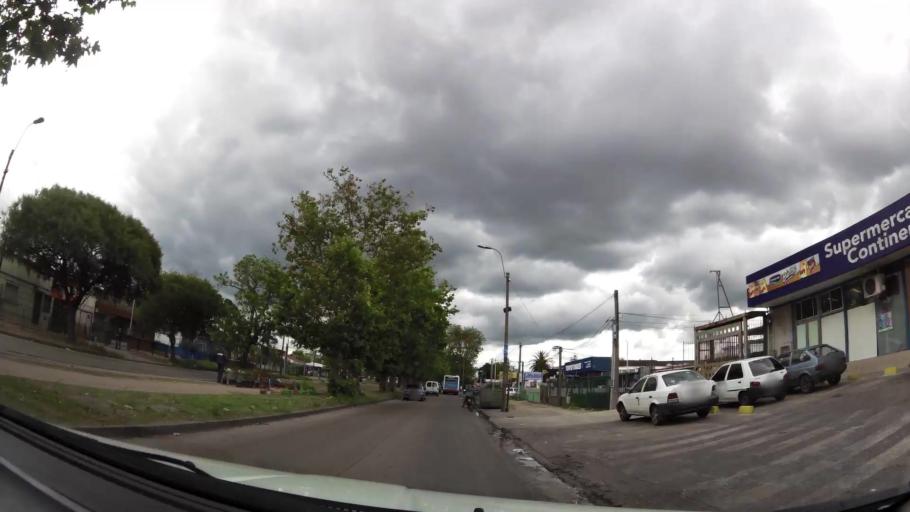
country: UY
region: Canelones
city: Toledo
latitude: -34.8166
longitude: -56.1389
